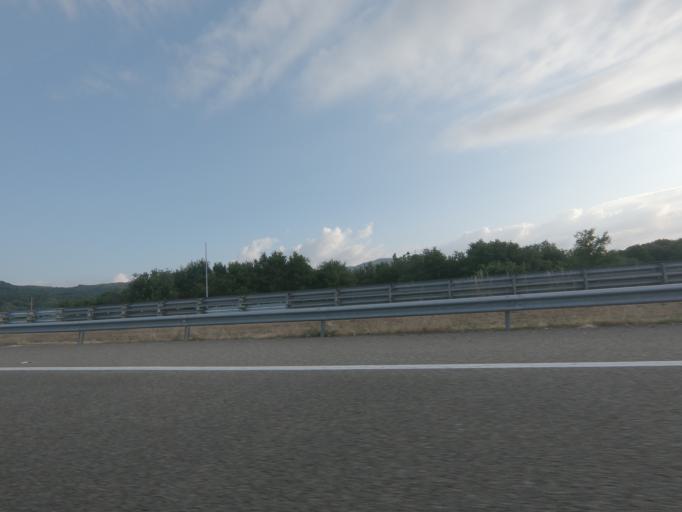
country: ES
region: Galicia
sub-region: Provincia de Ourense
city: Allariz
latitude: 42.1975
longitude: -7.7804
